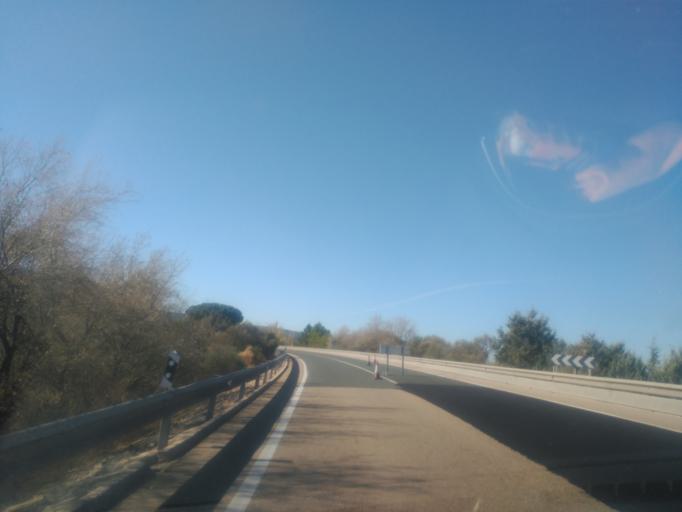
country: ES
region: Castille and Leon
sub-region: Provincia de Valladolid
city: Quintanilla de Onesimo
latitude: 41.6261
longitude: -4.3500
